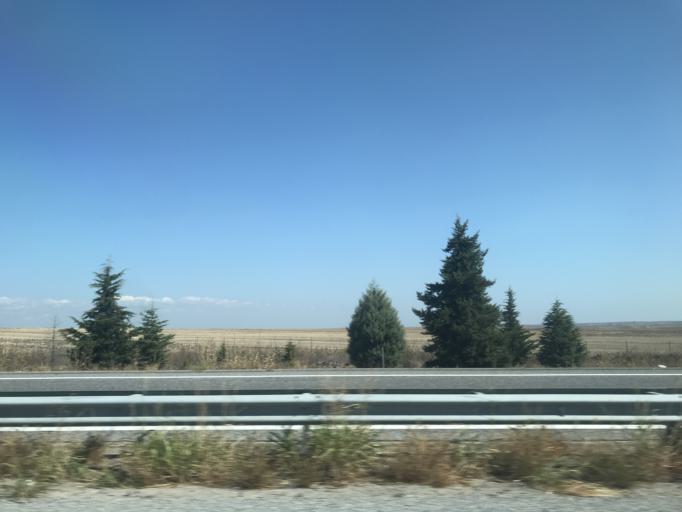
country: TR
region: Kirklareli
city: Luleburgaz
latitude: 41.4026
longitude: 27.3883
